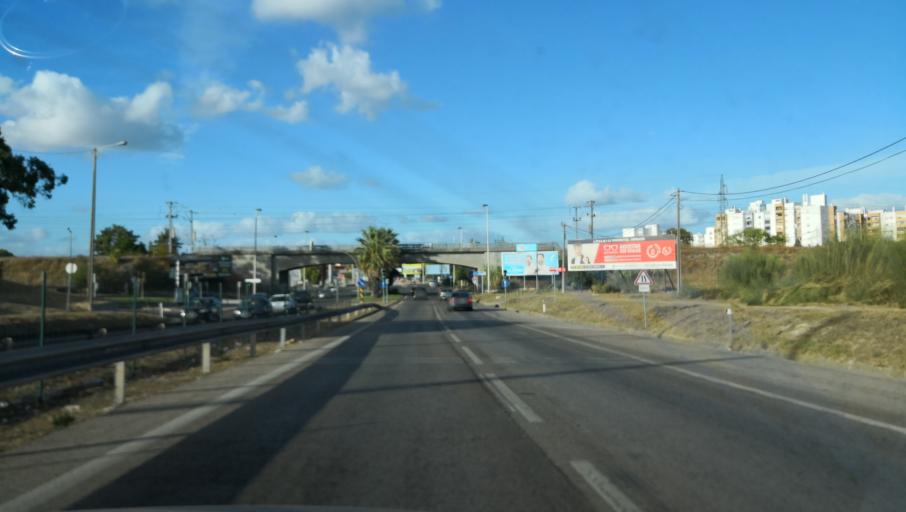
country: PT
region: Setubal
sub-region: Barreiro
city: Barreiro
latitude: 38.6602
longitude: -9.0548
